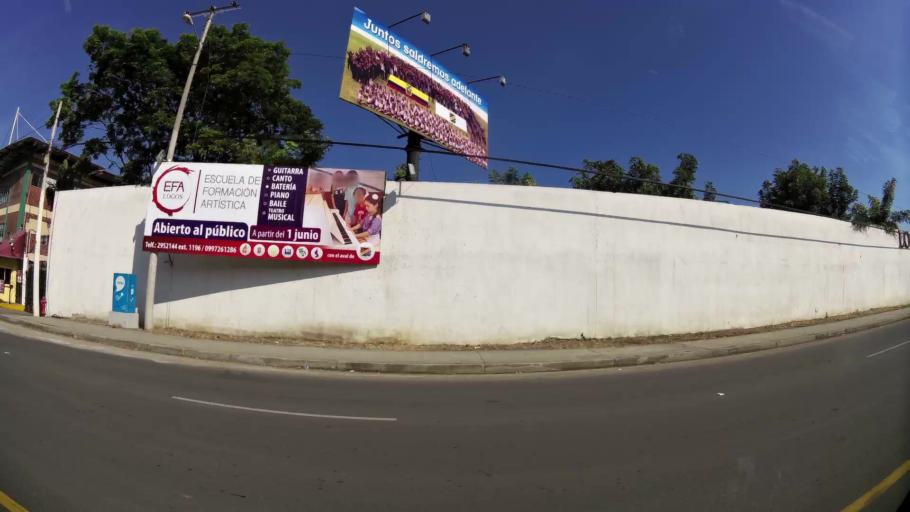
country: EC
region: Guayas
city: Santa Lucia
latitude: -2.1854
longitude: -80.0068
